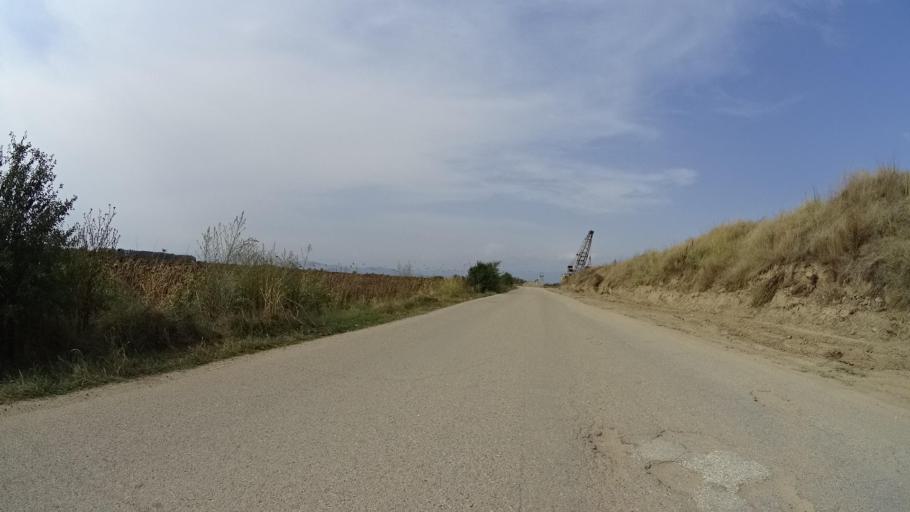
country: BG
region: Plovdiv
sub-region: Obshtina Kaloyanovo
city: Kaloyanovo
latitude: 42.3112
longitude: 24.7997
